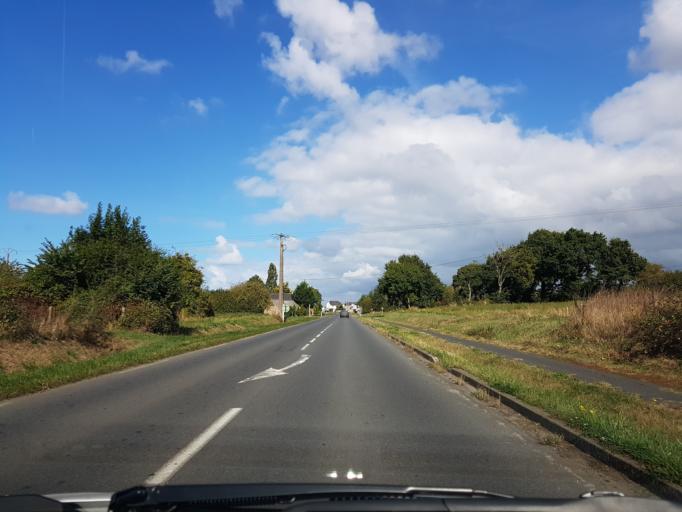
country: FR
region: Brittany
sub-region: Departement des Cotes-d'Armor
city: Pledran
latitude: 48.4798
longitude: -2.7495
